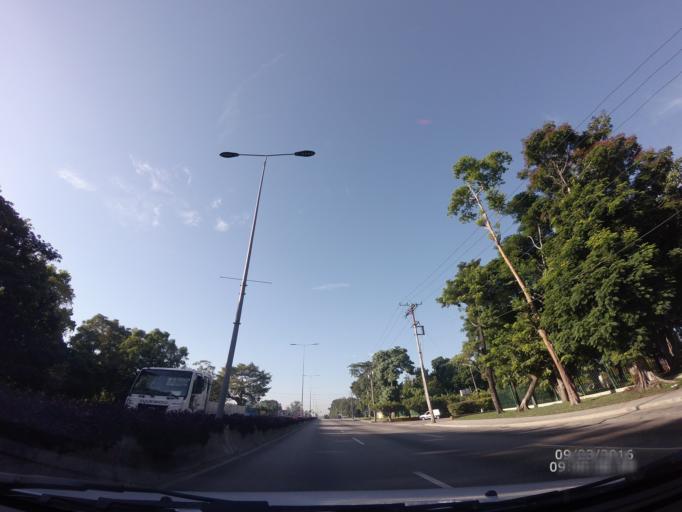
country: CU
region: La Habana
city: Arroyo Naranjo
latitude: 23.0547
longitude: -82.4034
